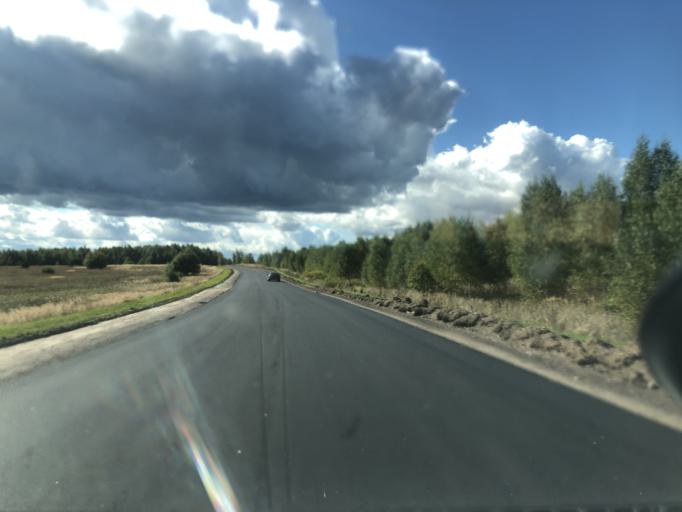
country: RU
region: Jaroslavl
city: Petrovsk
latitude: 56.9590
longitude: 39.3567
